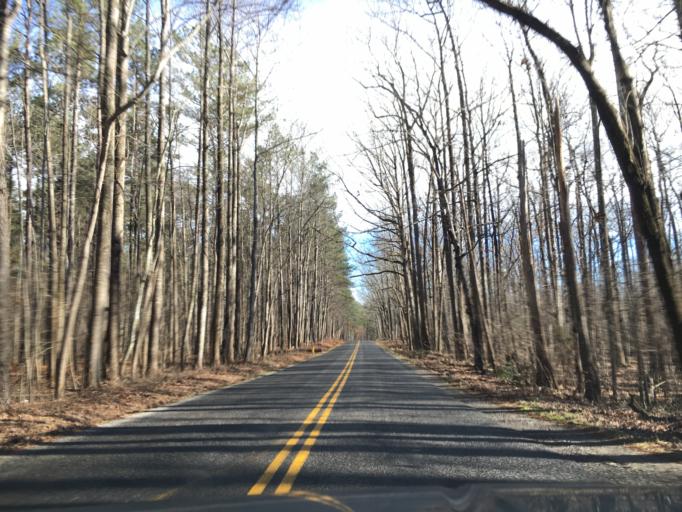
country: US
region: Virginia
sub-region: Amelia County
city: Amelia Court House
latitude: 37.4367
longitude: -78.0389
